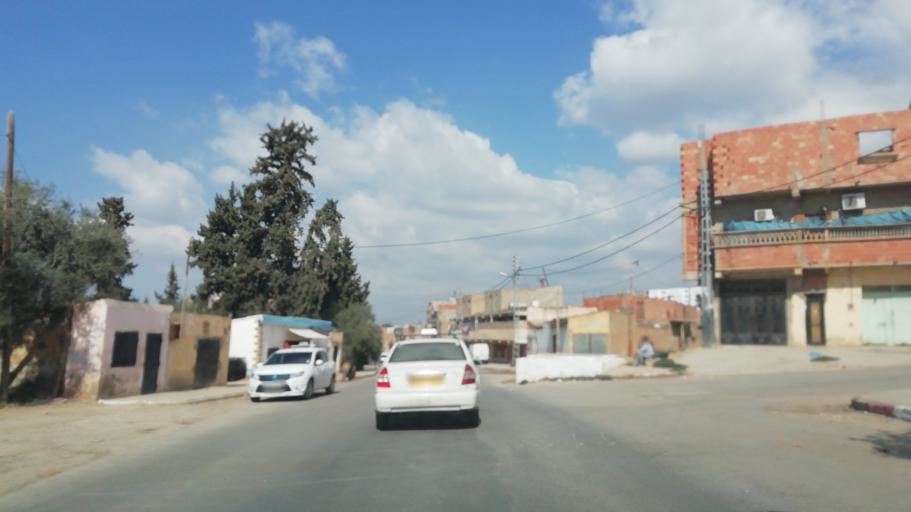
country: DZ
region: Mascara
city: Mascara
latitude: 35.5741
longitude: 0.0699
